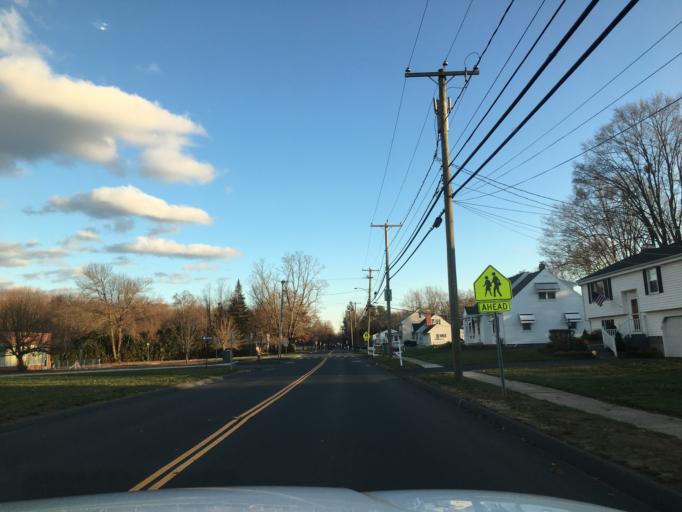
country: US
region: Connecticut
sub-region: Hartford County
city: Southwood Acres
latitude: 41.9619
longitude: -72.5774
